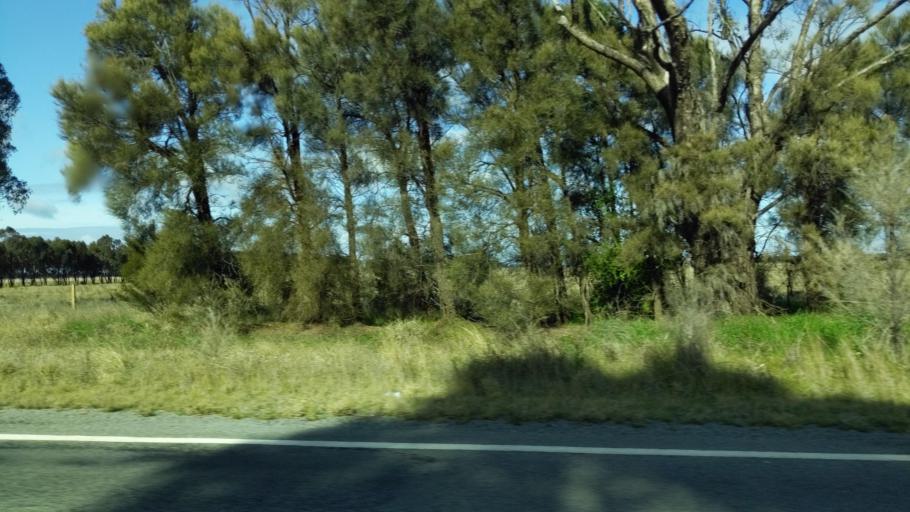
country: AU
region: New South Wales
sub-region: Narrandera
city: Narrandera
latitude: -34.7564
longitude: 146.8643
